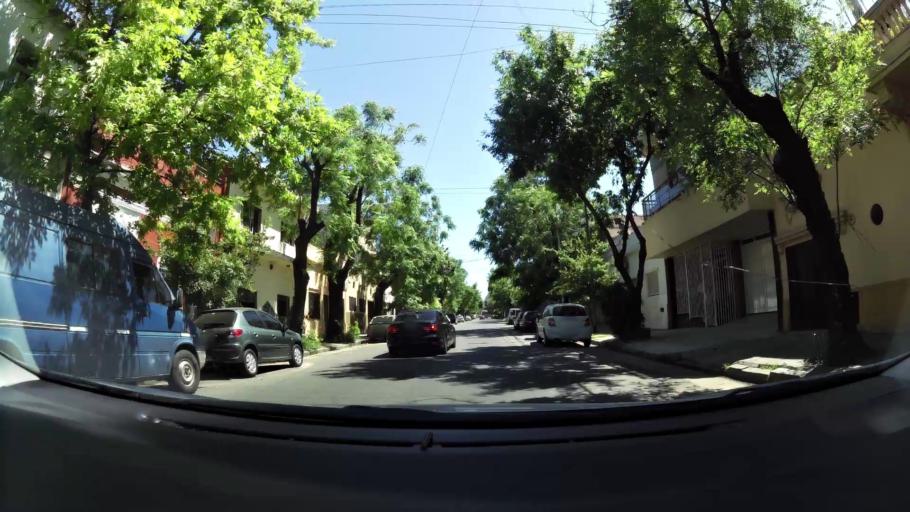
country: AR
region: Buenos Aires F.D.
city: Buenos Aires
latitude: -34.6354
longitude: -58.4194
